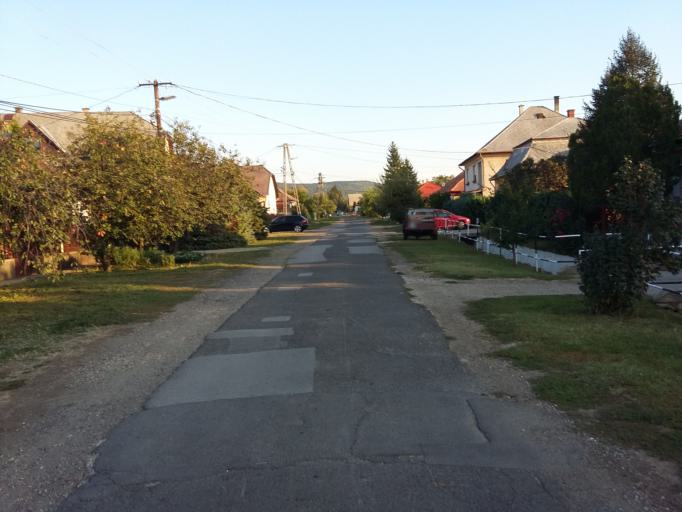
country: HU
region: Borsod-Abauj-Zemplen
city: Bekecs
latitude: 48.1605
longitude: 21.1821
